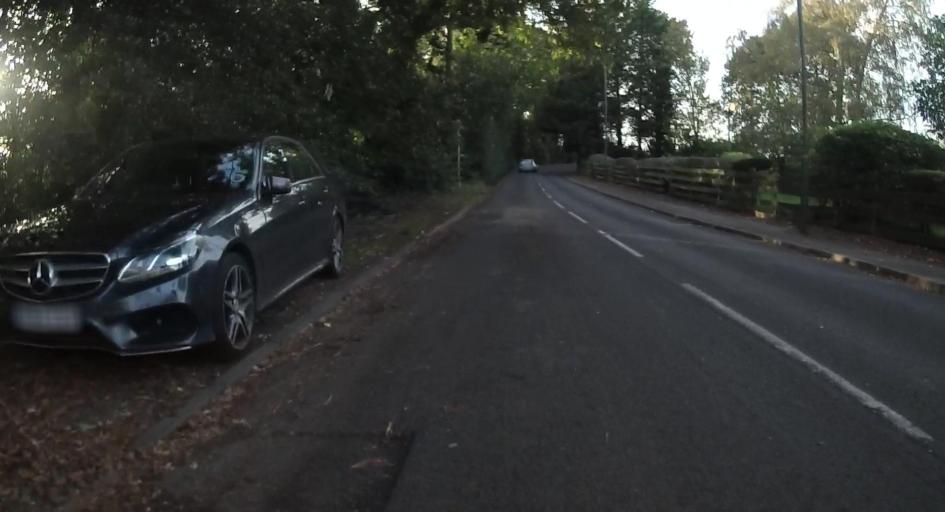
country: GB
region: England
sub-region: Surrey
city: Frimley
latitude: 51.3000
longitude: -0.7239
